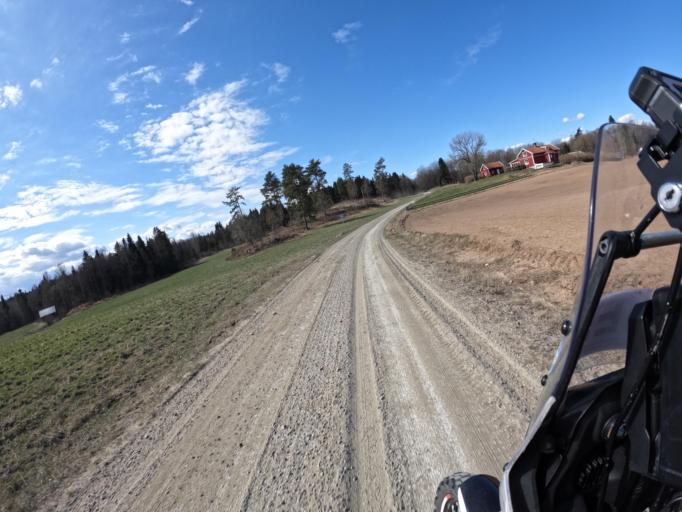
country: SE
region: Joenkoeping
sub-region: Mullsjo Kommun
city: Mullsjoe
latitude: 57.9544
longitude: 13.6463
